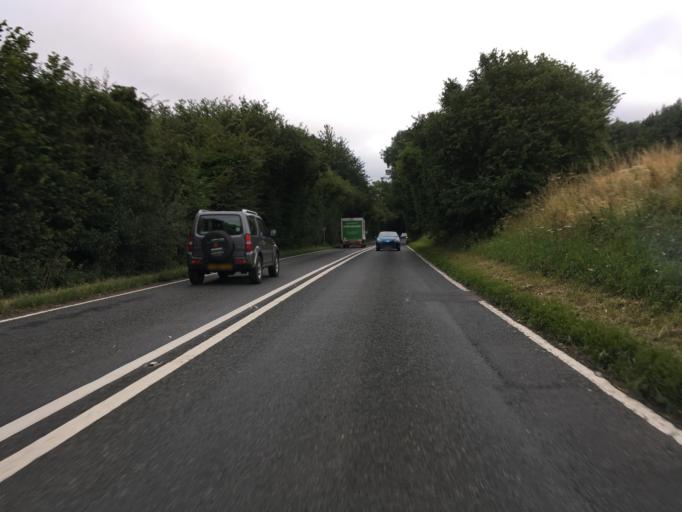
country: GB
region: England
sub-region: Hampshire
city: Four Marks
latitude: 51.0252
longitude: -1.0264
